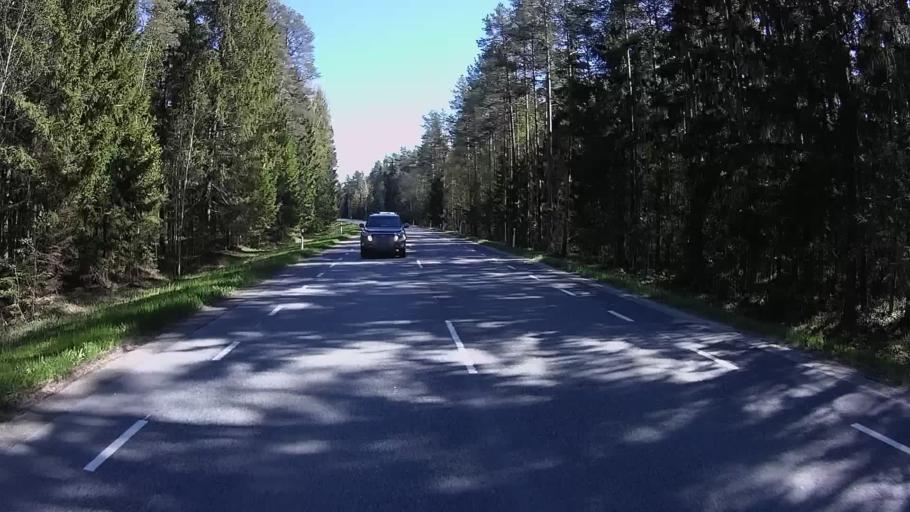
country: EE
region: Harju
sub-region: Loksa linn
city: Loksa
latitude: 59.5562
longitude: 25.7263
